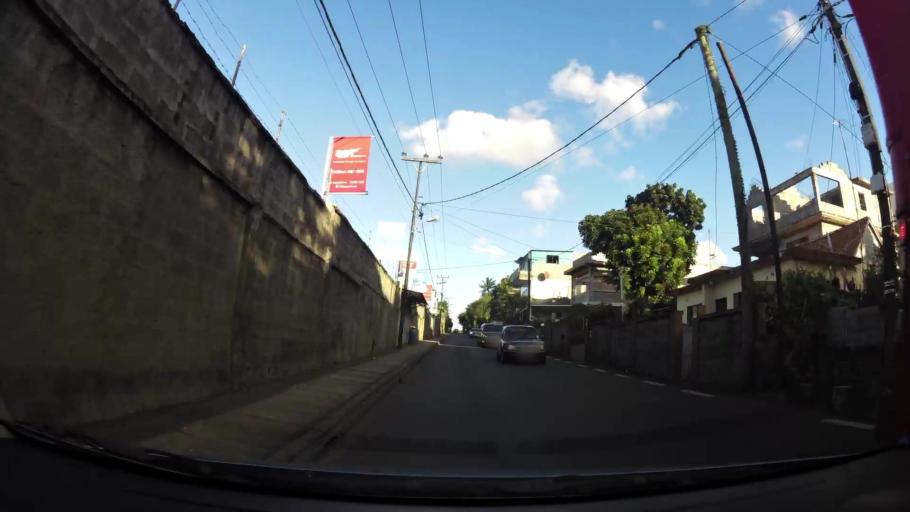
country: MU
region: Plaines Wilhems
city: Ebene
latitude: -20.2387
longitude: 57.4640
